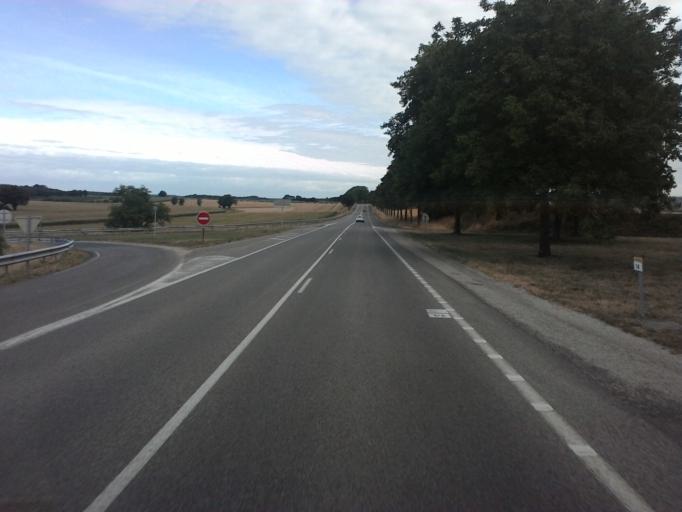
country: FR
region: Rhone-Alpes
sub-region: Departement de l'Ain
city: Saint-Martin-du-Mont
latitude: 46.0955
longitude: 5.3121
